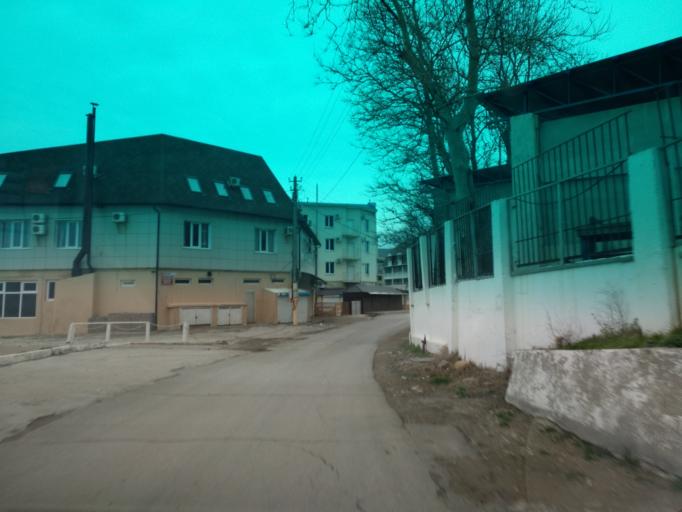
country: RU
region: Krasnodarskiy
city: Novomikhaylovskiy
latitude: 44.2381
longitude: 38.8372
